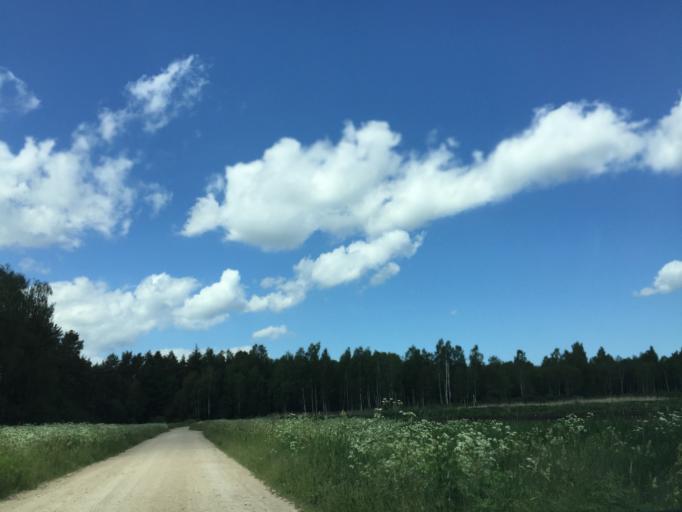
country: LV
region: Olaine
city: Olaine
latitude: 56.8543
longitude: 23.9466
